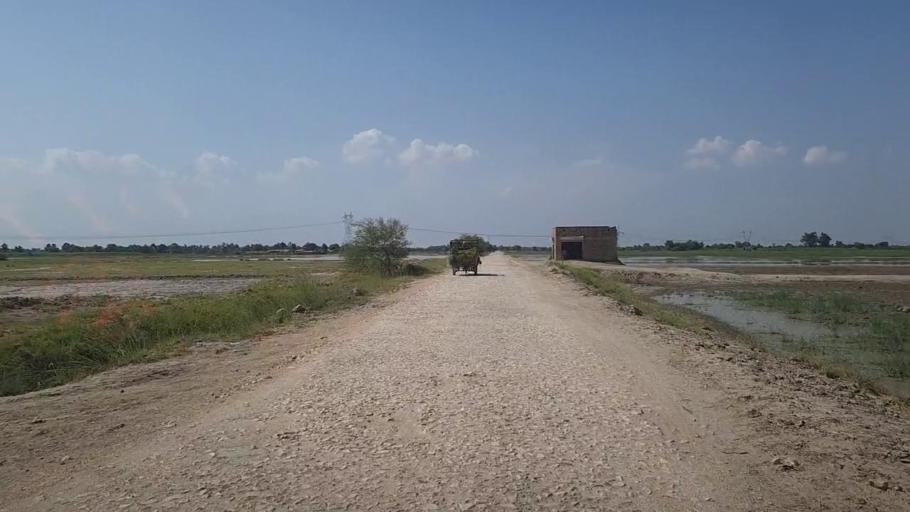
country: PK
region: Sindh
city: Khairpur
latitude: 28.1034
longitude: 69.6243
